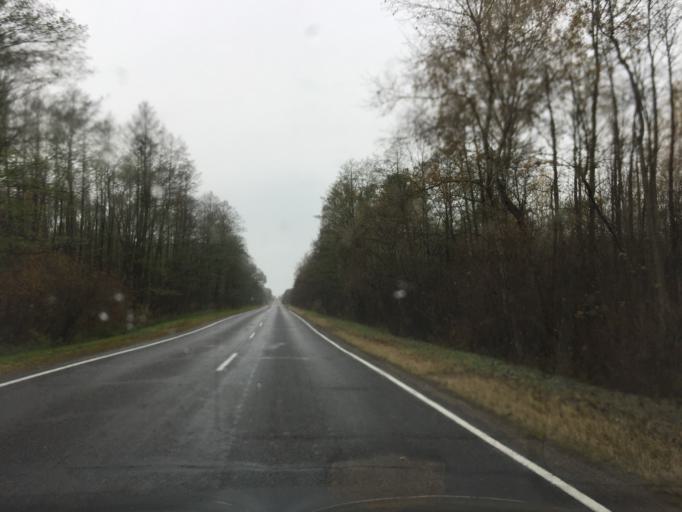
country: BY
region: Gomel
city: Karma
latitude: 53.3164
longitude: 30.7540
